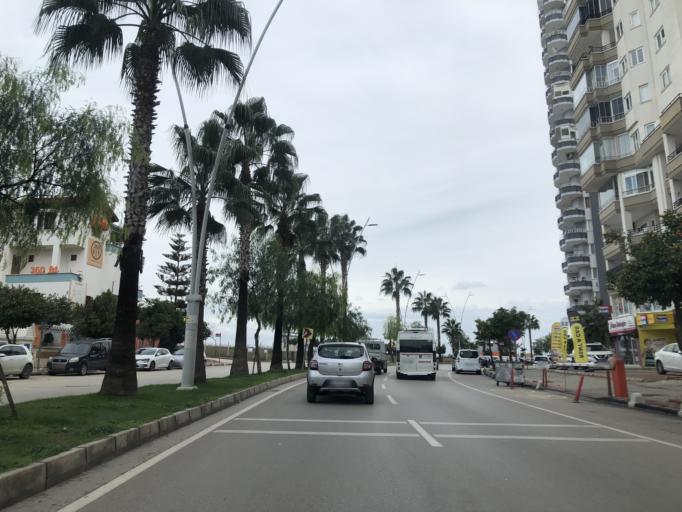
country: TR
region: Adana
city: Adana
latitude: 37.0570
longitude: 35.2846
